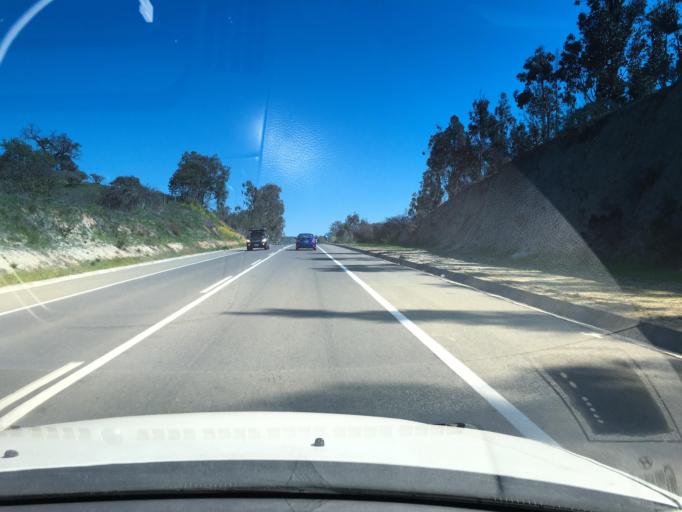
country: CL
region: Valparaiso
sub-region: San Antonio Province
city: El Tabo
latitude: -33.3960
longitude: -71.4902
